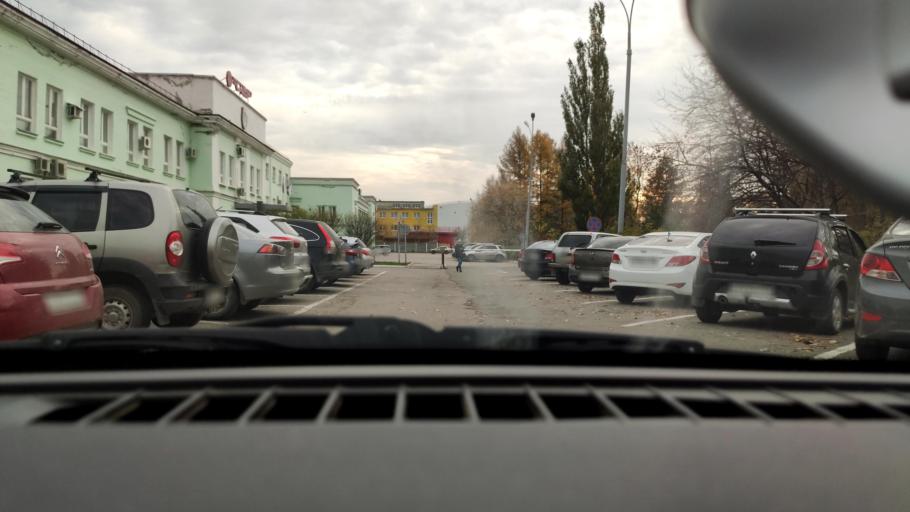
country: RU
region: Perm
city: Perm
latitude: 57.9647
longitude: 56.2469
